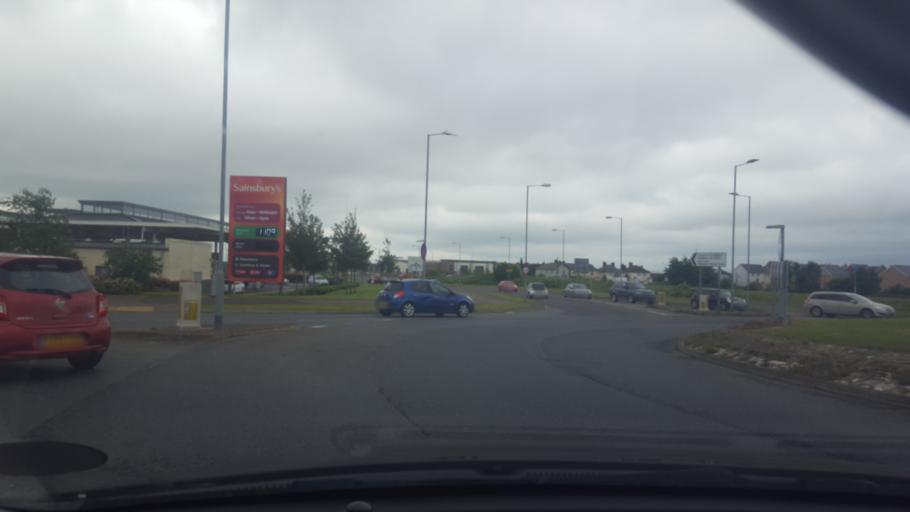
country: GB
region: England
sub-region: Essex
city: Eight Ash Green
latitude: 51.8874
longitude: 0.8273
